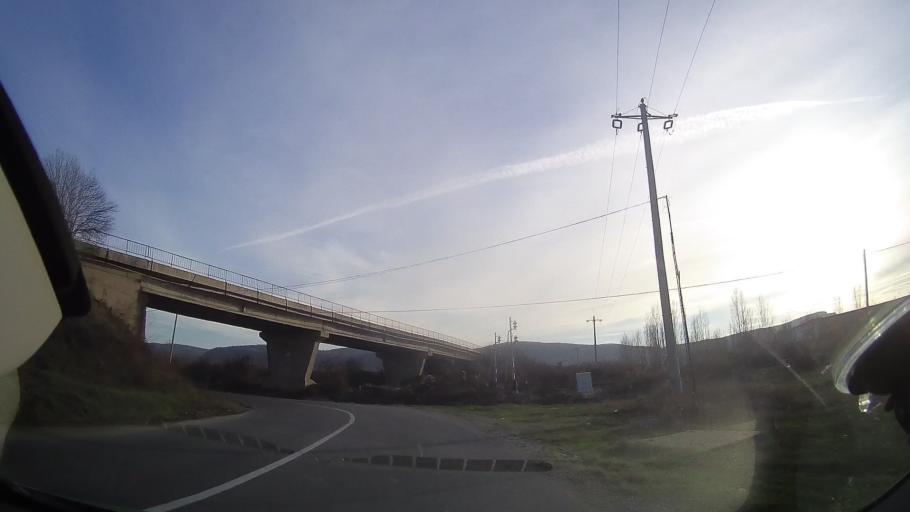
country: RO
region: Bihor
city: Lugasu de Jos
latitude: 47.0412
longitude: 22.3454
